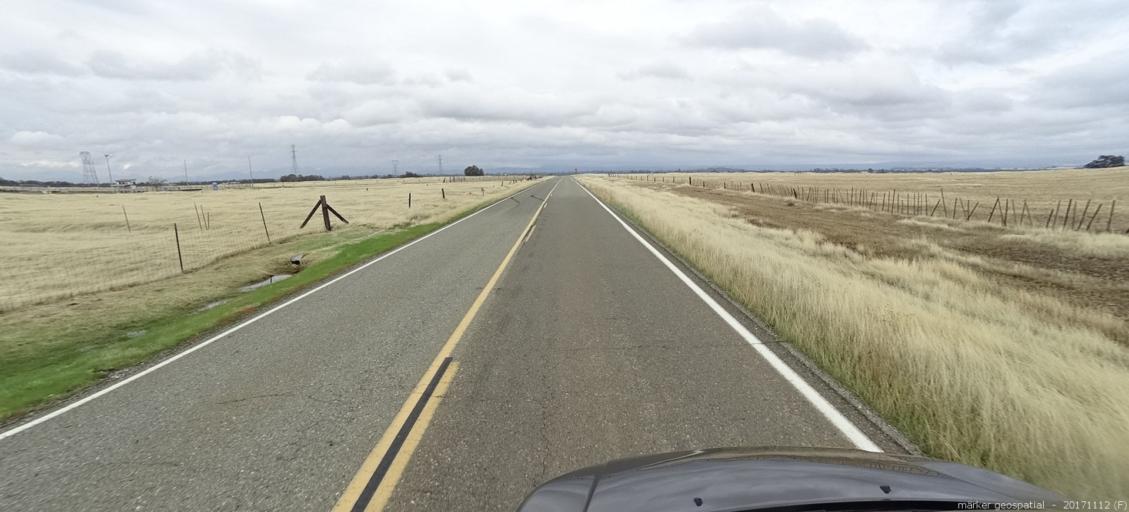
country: US
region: California
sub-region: Shasta County
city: Palo Cedro
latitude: 40.5254
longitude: -122.1769
